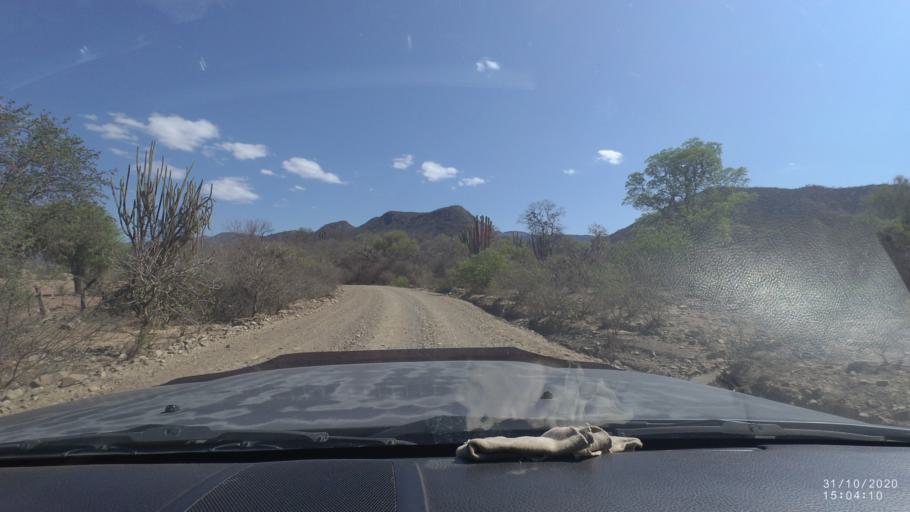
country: BO
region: Cochabamba
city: Aiquile
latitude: -18.2807
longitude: -64.8041
